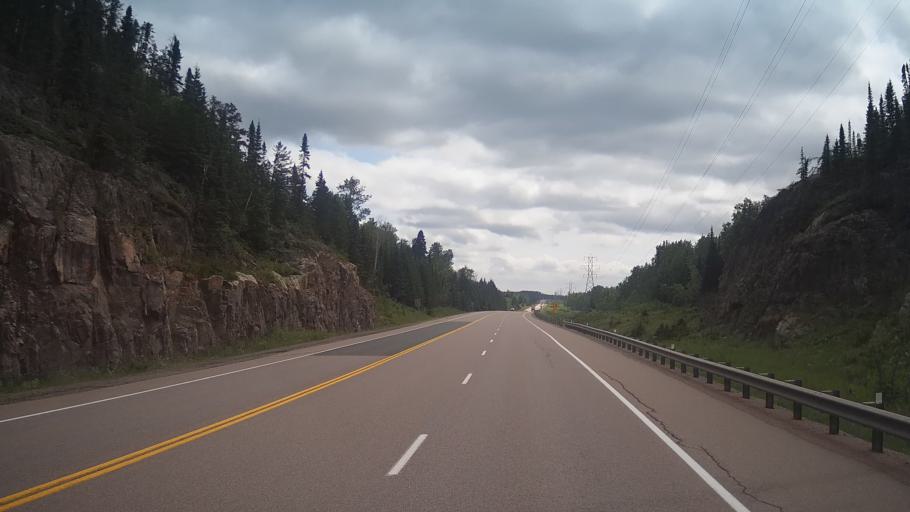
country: CA
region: Ontario
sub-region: Thunder Bay District
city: Thunder Bay
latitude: 48.7046
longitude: -88.6282
